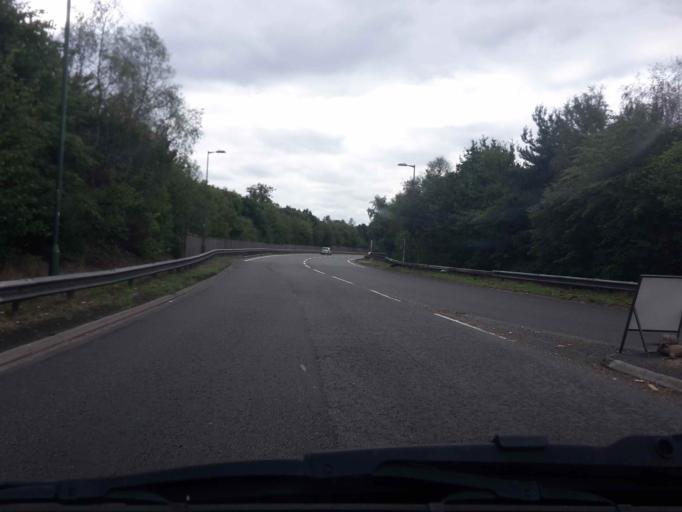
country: GB
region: England
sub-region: Hampshire
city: Fleet
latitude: 51.3005
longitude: -0.7971
